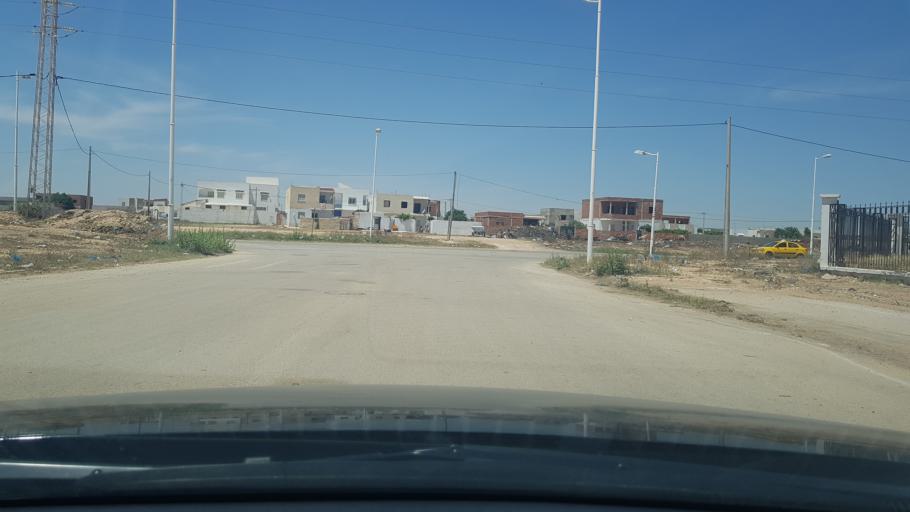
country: TN
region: Safaqis
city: Al Qarmadah
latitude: 34.8359
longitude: 10.7483
